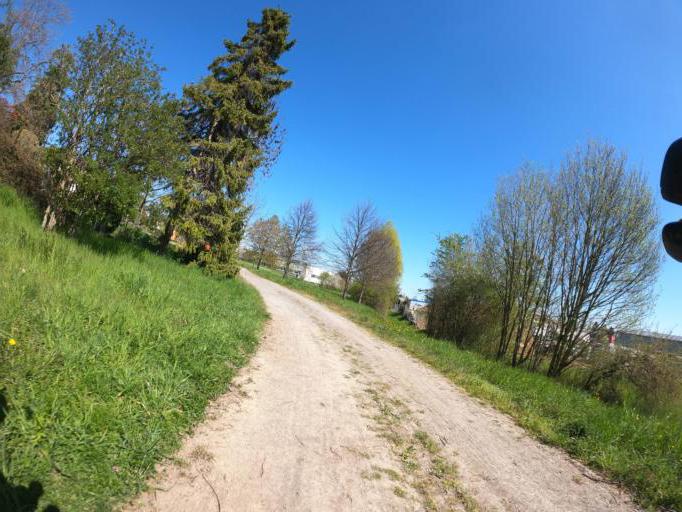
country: DE
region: Baden-Wuerttemberg
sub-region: Karlsruhe Region
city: Eutingen
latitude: 48.9127
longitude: 8.7206
